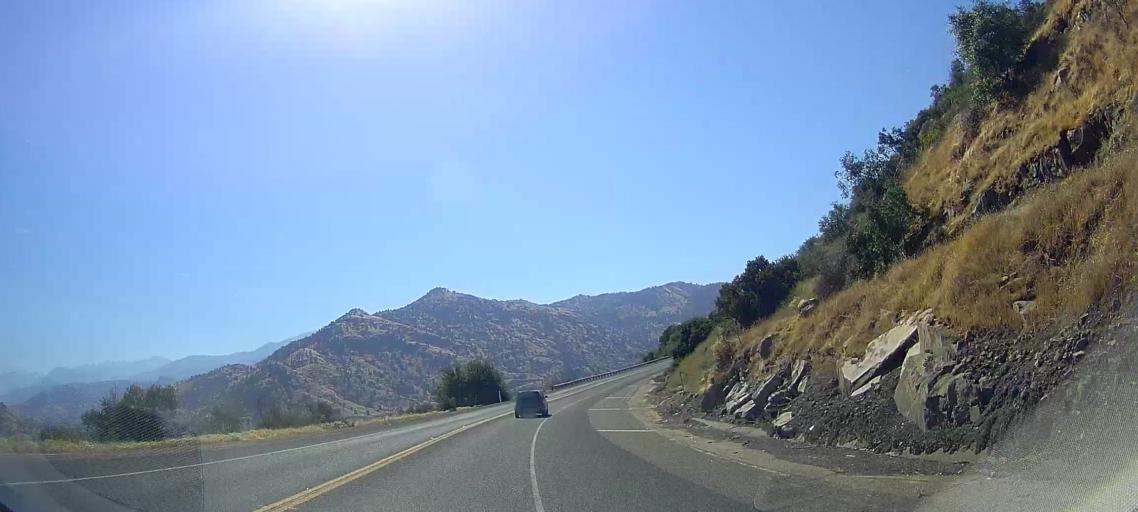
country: US
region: California
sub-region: Tulare County
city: Three Rivers
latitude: 36.3988
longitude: -118.9726
